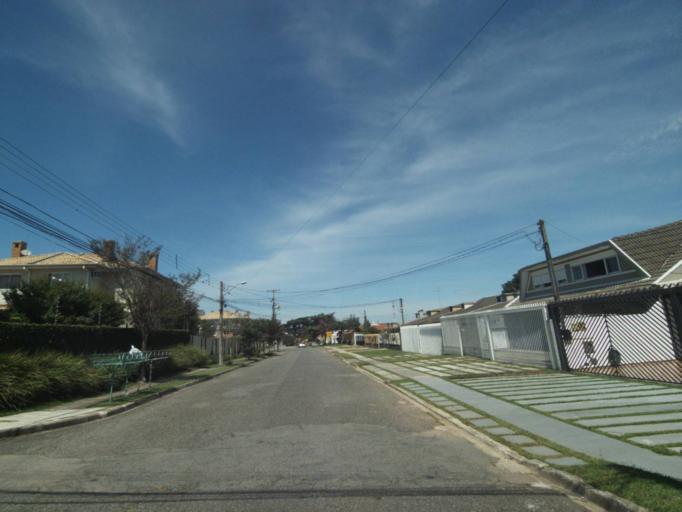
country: BR
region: Parana
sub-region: Curitiba
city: Curitiba
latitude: -25.4621
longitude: -49.2406
